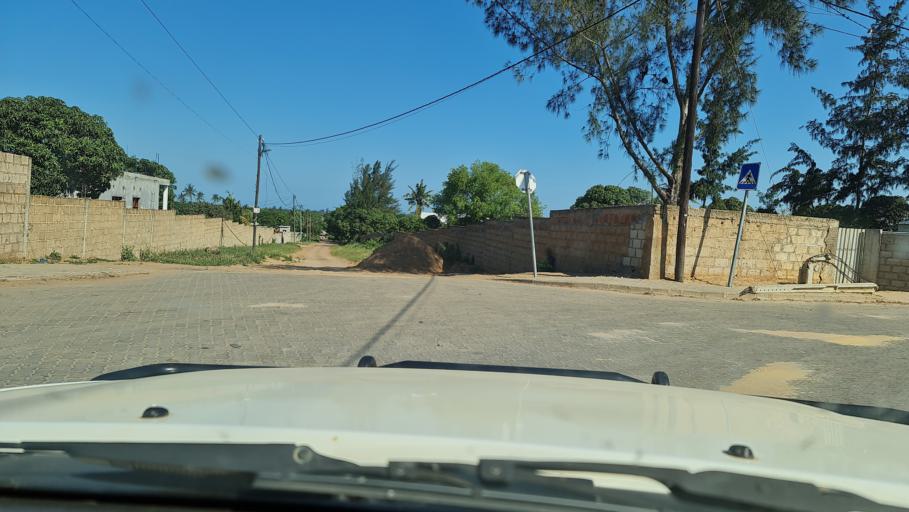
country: MZ
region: Maputo City
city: Maputo
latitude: -25.8427
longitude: 32.6432
